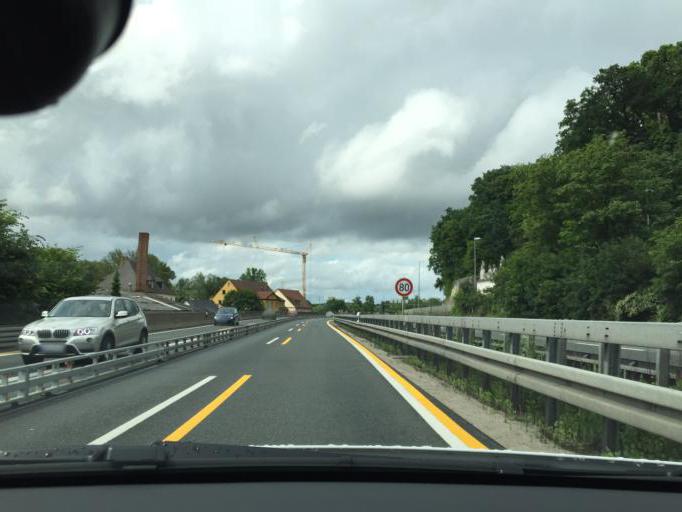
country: DE
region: Bavaria
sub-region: Regierungsbezirk Mittelfranken
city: Erlangen
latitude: 49.6090
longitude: 10.9986
